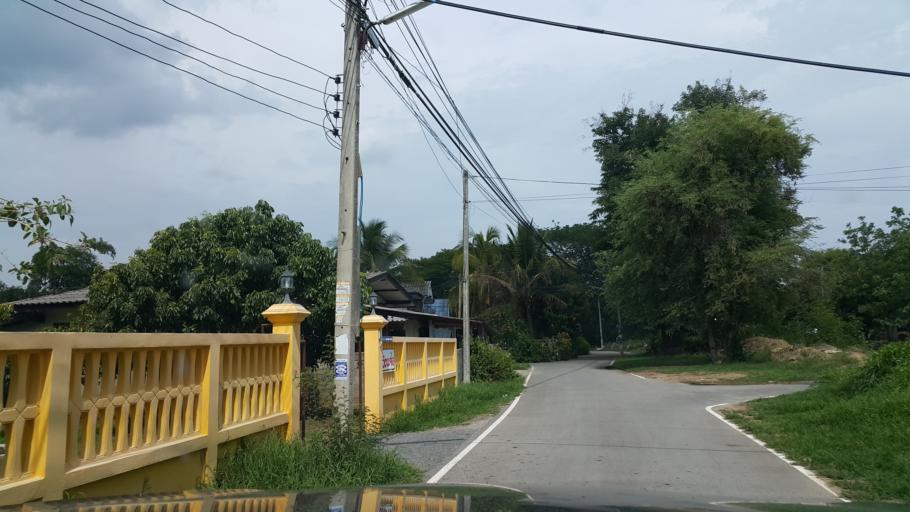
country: TH
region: Chiang Mai
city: San Kamphaeng
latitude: 18.7320
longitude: 99.1251
